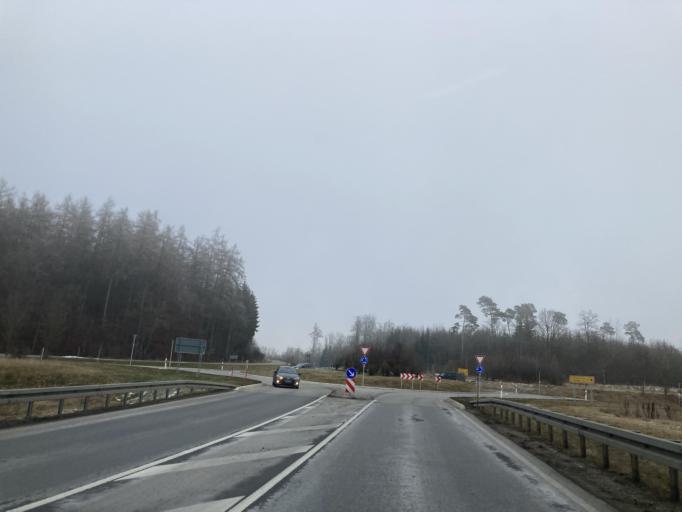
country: DE
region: Baden-Wuerttemberg
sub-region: Freiburg Region
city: Emmingen-Liptingen
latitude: 47.9497
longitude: 8.8925
